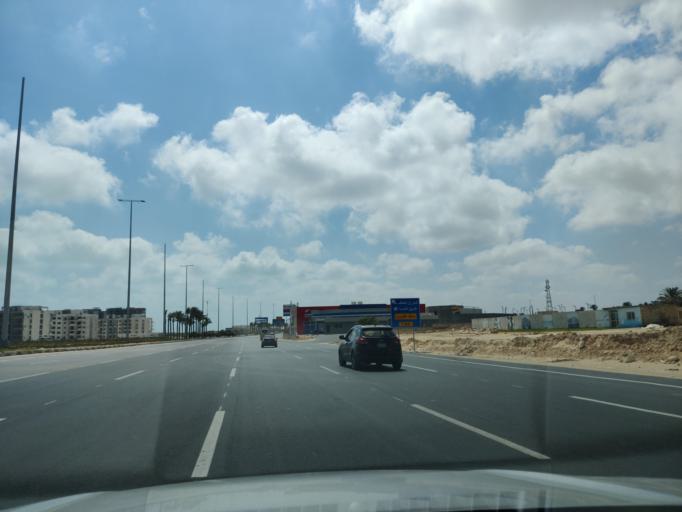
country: EG
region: Muhafazat Matruh
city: Al `Alamayn
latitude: 30.8453
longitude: 28.9388
